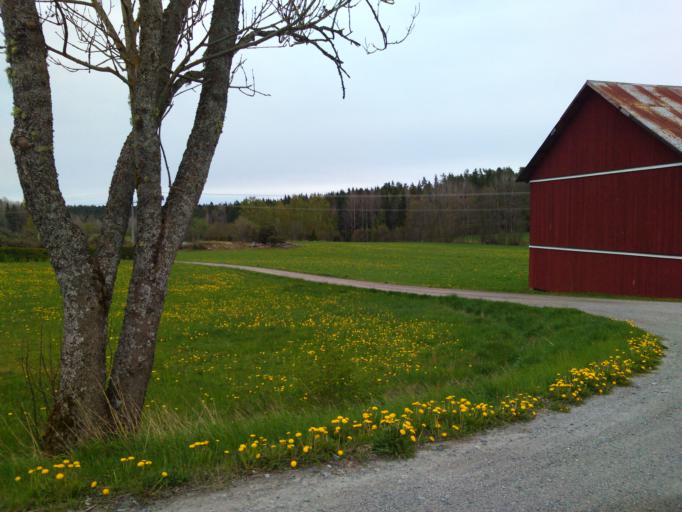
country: SE
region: Stockholm
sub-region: Norrtalje Kommun
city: Norrtalje
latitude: 59.6591
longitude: 18.6658
